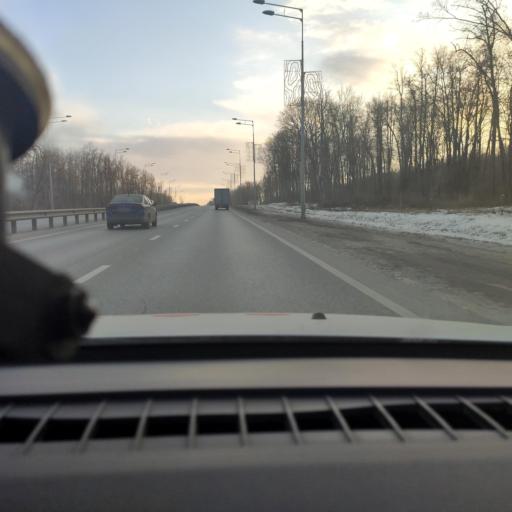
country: RU
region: Samara
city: Novosemeykino
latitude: 53.3214
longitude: 50.2303
